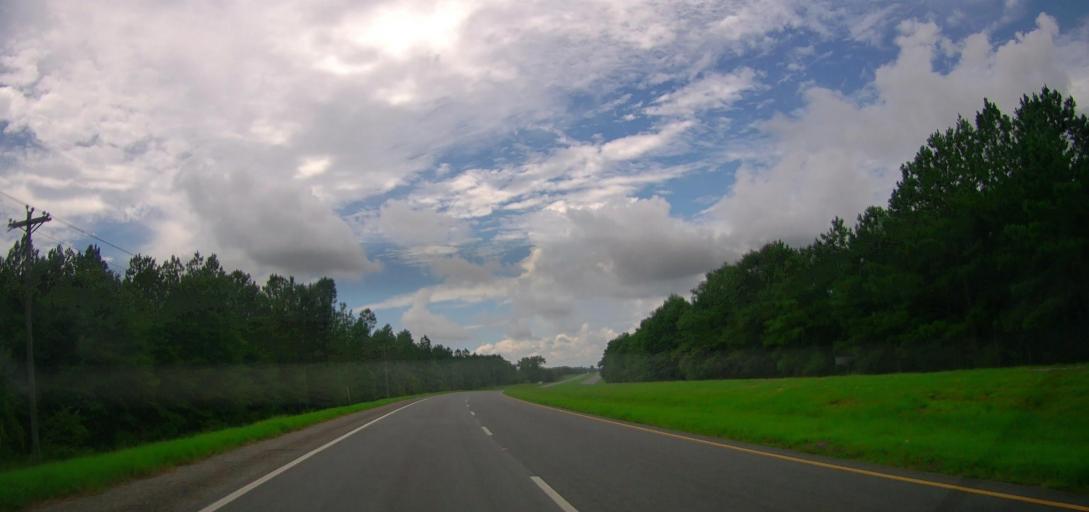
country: US
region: Georgia
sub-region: Dodge County
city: Eastman
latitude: 32.1088
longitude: -83.0911
